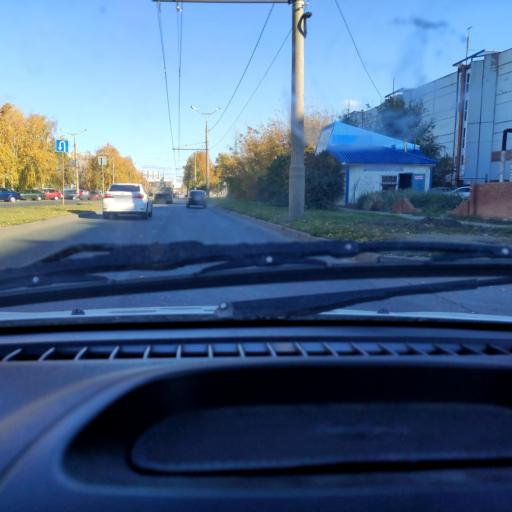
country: RU
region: Samara
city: Tol'yatti
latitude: 53.5328
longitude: 49.4313
